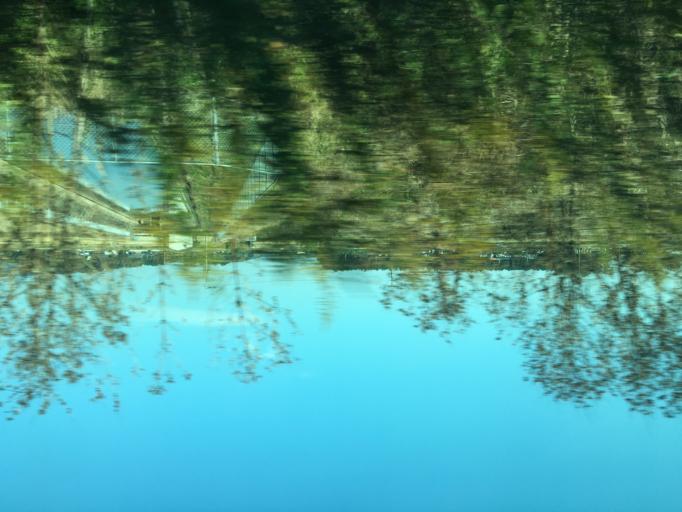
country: JP
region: Ibaraki
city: Iwase
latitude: 36.3318
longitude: 140.0464
